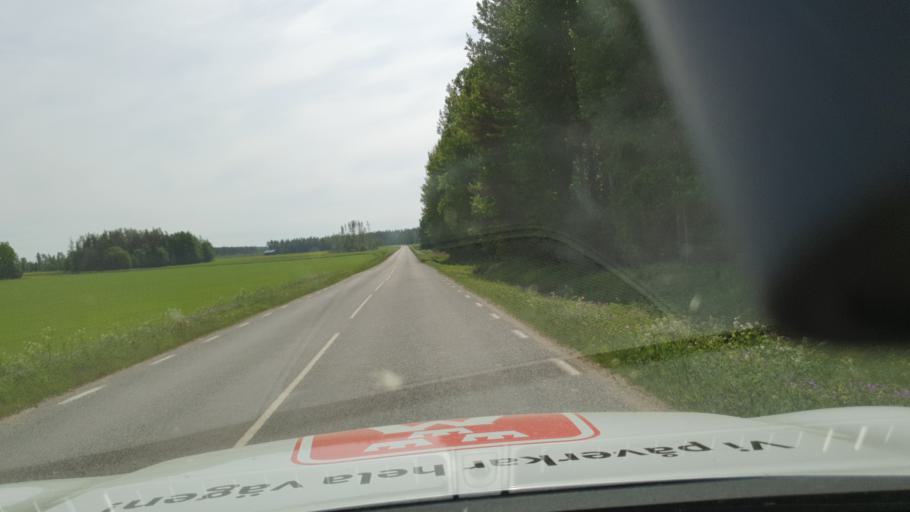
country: SE
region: Vaesterbotten
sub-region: Robertsfors Kommun
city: Robertsfors
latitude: 64.2979
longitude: 20.8833
